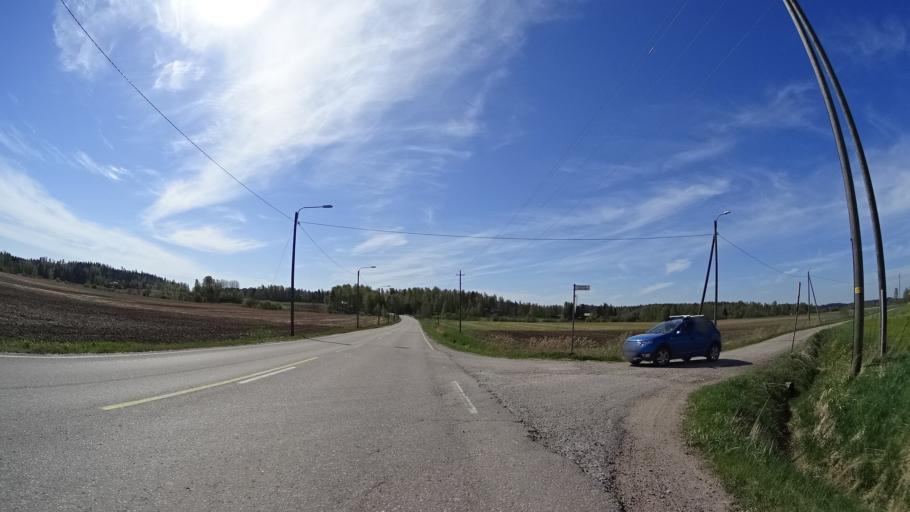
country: FI
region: Uusimaa
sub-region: Helsinki
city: Nurmijaervi
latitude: 60.3616
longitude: 24.8570
